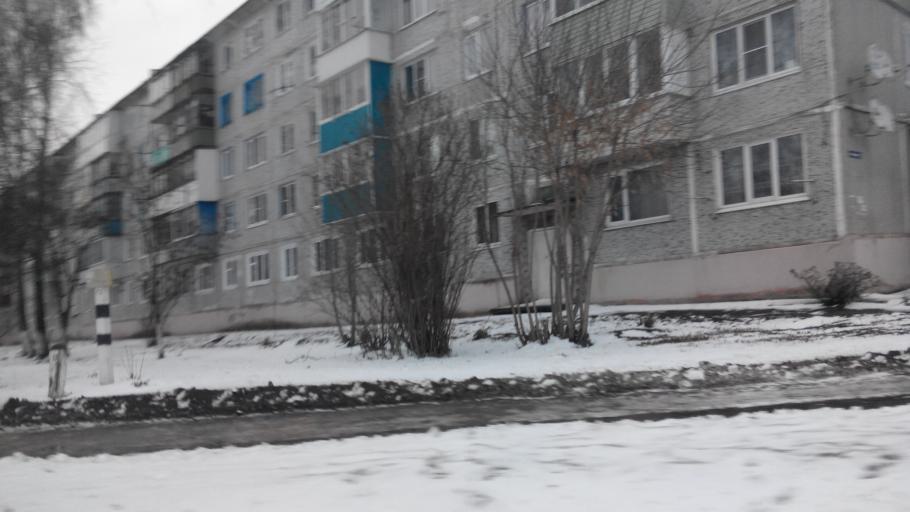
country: RU
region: Tula
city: Podlesnyy
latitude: 53.9656
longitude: 38.2884
